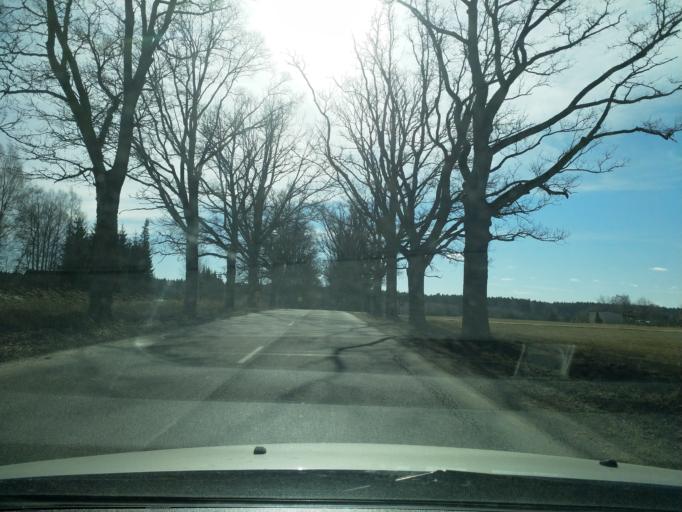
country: LV
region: Valmieras Rajons
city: Valmiera
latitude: 57.5160
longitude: 25.4210
